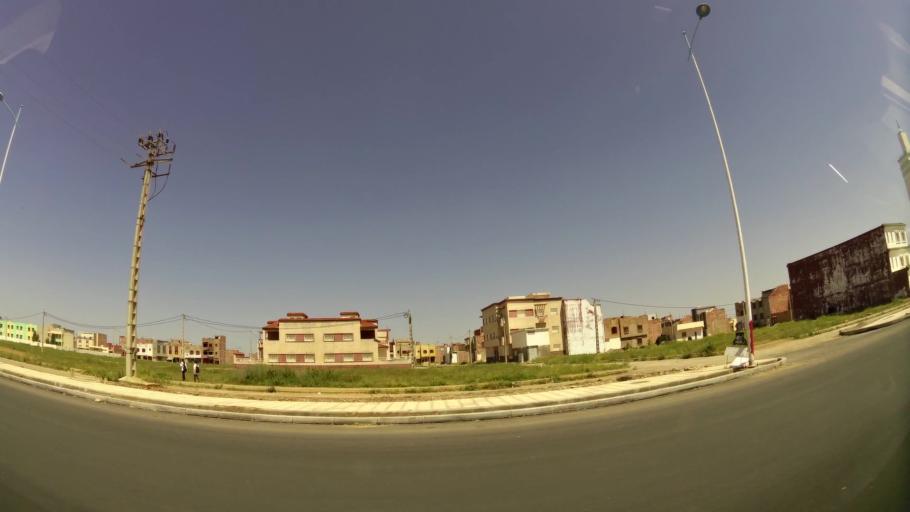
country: MA
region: Rabat-Sale-Zemmour-Zaer
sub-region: Khemisset
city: Khemisset
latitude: 33.8080
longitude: -6.0822
